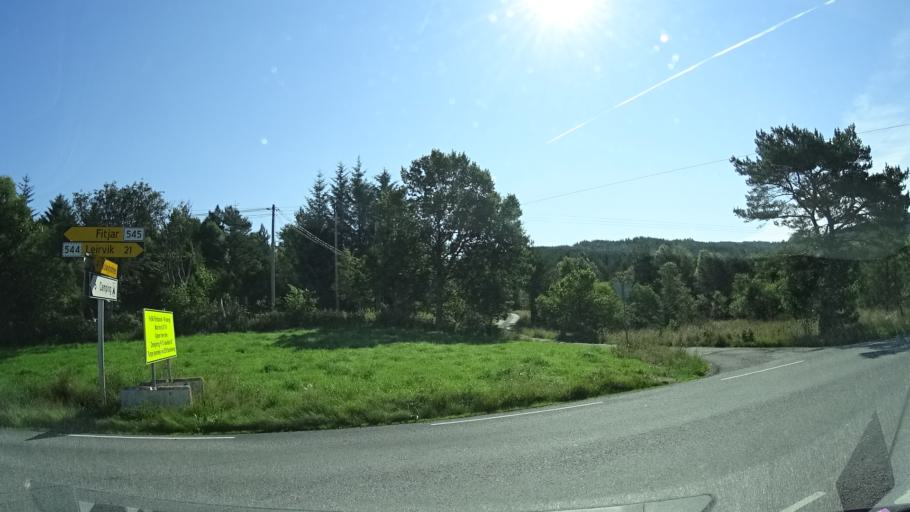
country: NO
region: Hordaland
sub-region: Fitjar
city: Fitjar
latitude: 59.8662
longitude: 5.3490
